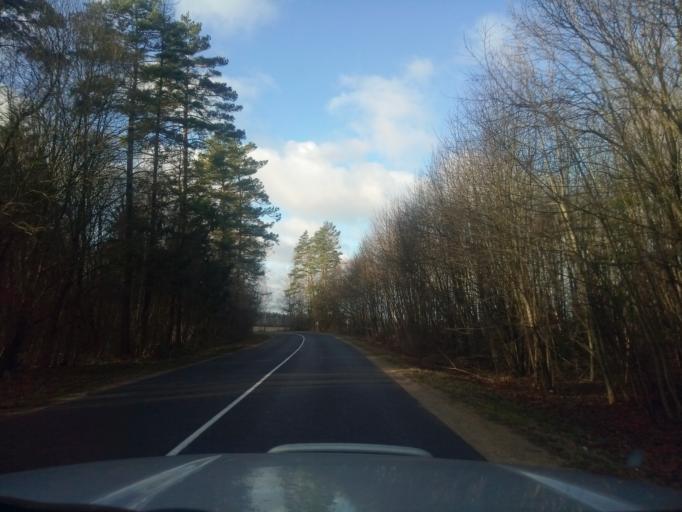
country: BY
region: Minsk
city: Kapyl'
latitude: 53.1758
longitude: 27.0094
